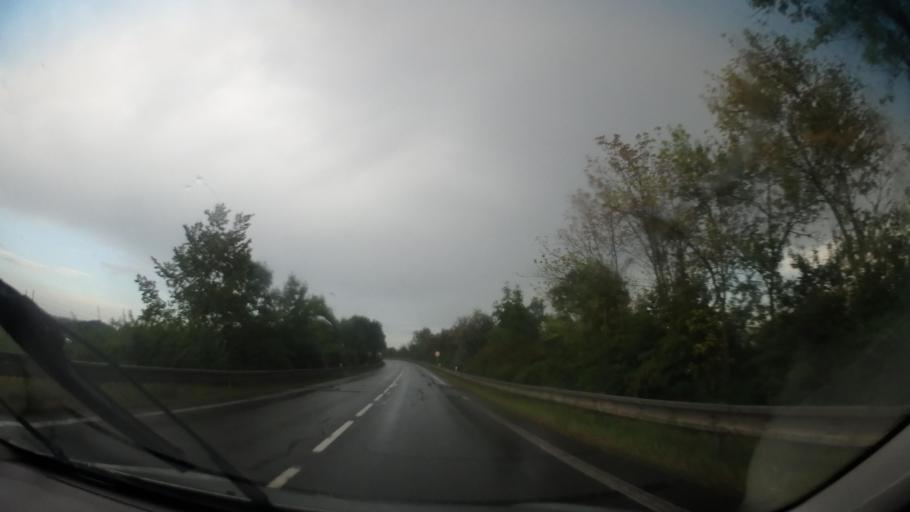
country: CZ
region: Olomoucky
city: Cervenka
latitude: 49.7126
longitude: 17.1152
